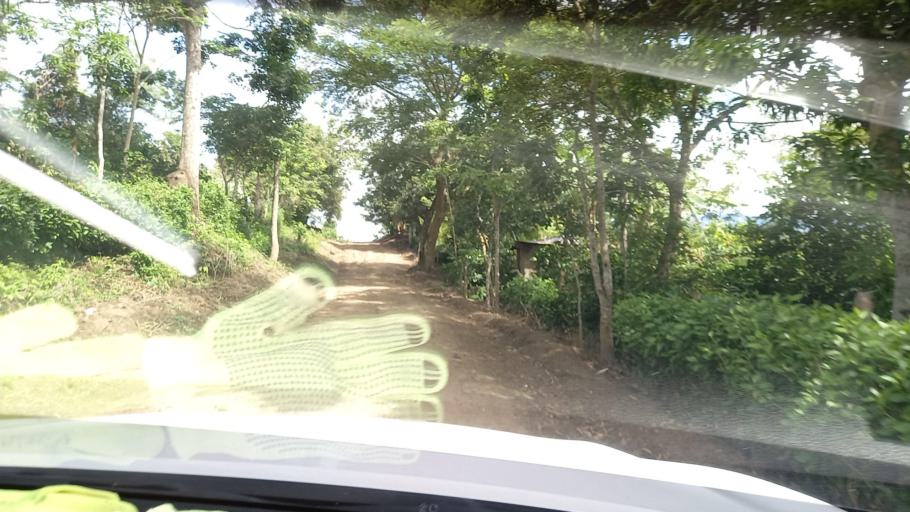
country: NI
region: Jinotega
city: San Jose de Bocay
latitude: 13.4062
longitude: -85.7016
